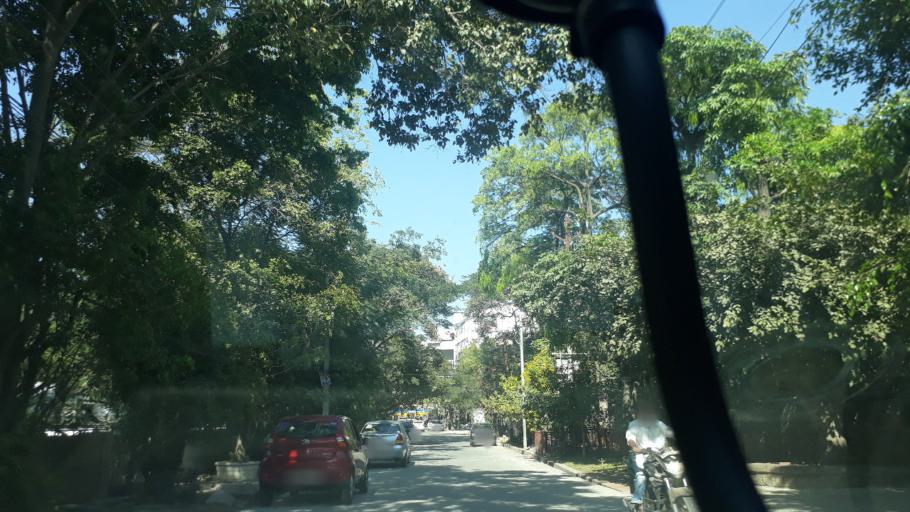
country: IN
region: Telangana
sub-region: Rangareddi
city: Kukatpalli
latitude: 17.4297
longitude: 78.4071
